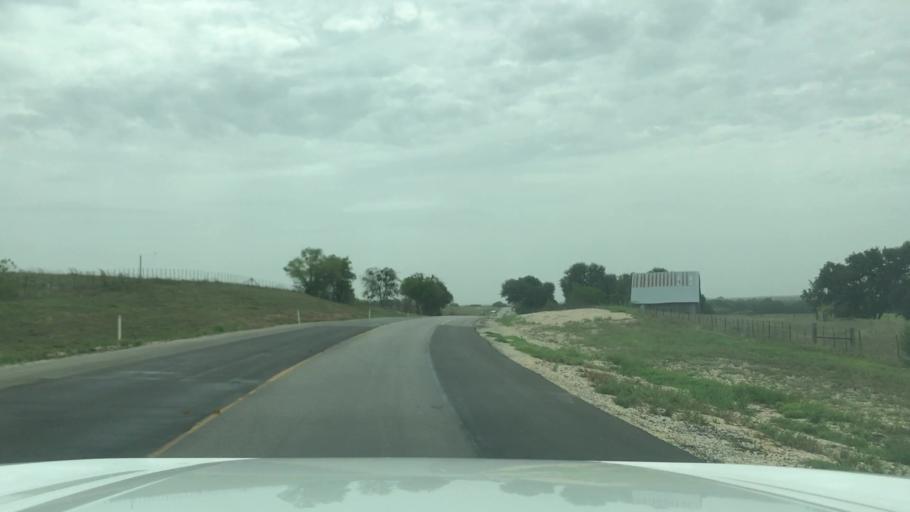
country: US
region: Texas
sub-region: Erath County
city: Dublin
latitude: 32.0716
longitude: -98.2220
